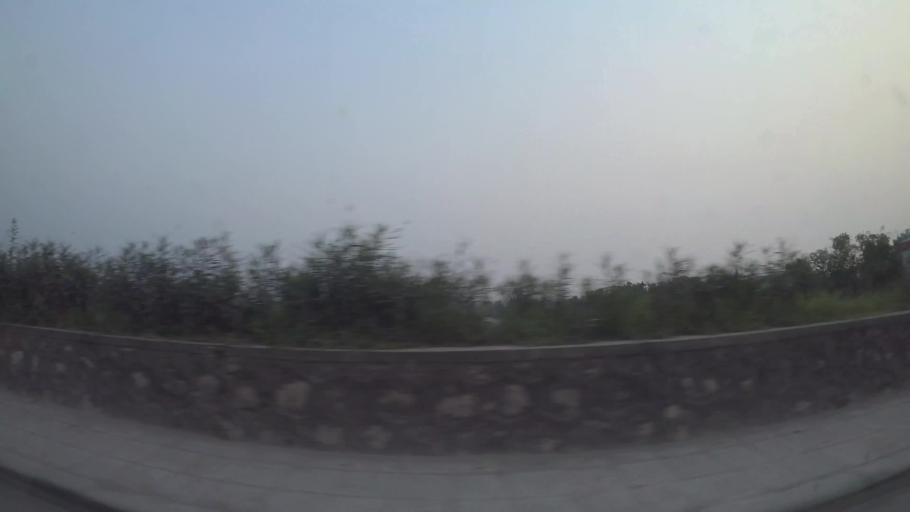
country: VN
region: Ha Noi
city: Van Dien
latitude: 20.9718
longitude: 105.8856
